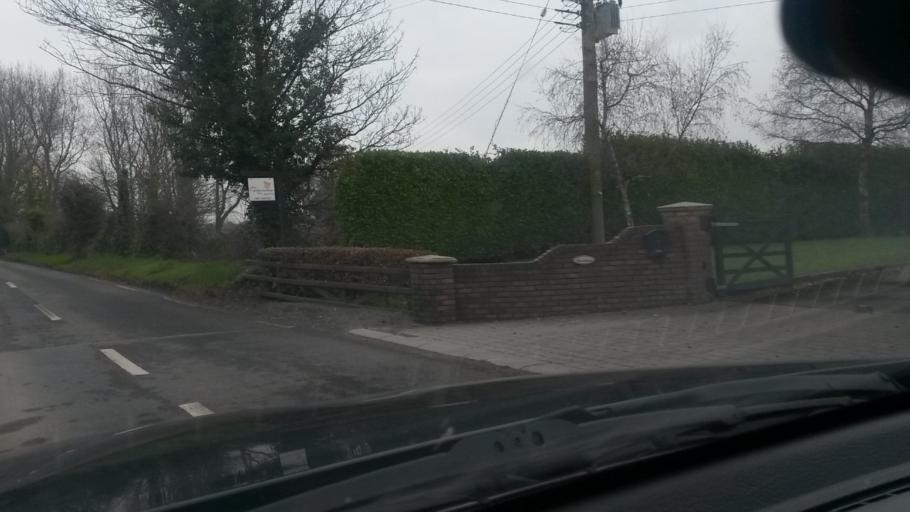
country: IE
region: Leinster
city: Donaghmede
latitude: 53.4243
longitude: -6.1695
